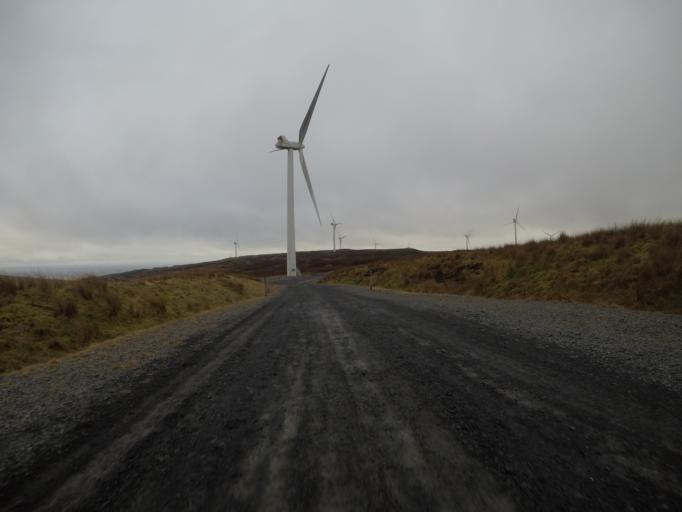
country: GB
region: Scotland
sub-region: North Ayrshire
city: Fairlie
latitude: 55.7562
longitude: -4.7950
